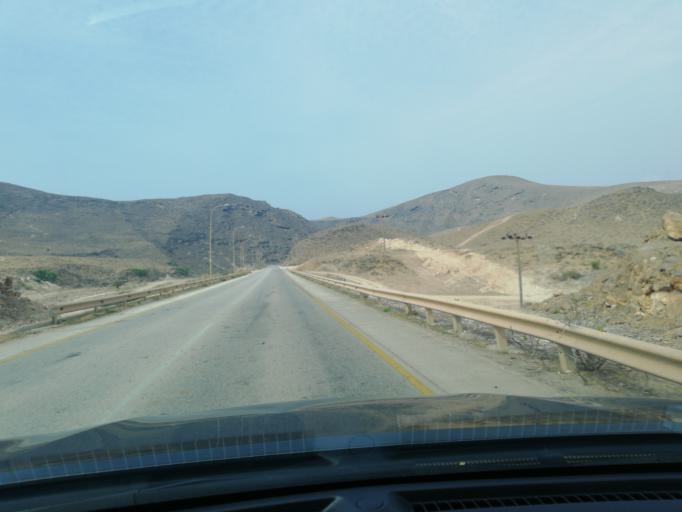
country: OM
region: Zufar
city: Salalah
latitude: 16.9035
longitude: 53.8211
